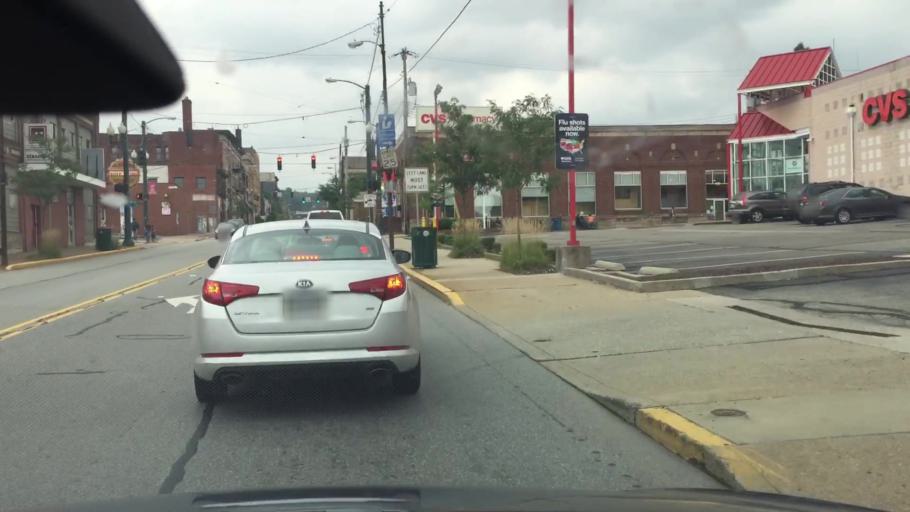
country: US
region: Pennsylvania
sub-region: Allegheny County
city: Wilkinsburg
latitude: 40.4443
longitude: -79.8866
